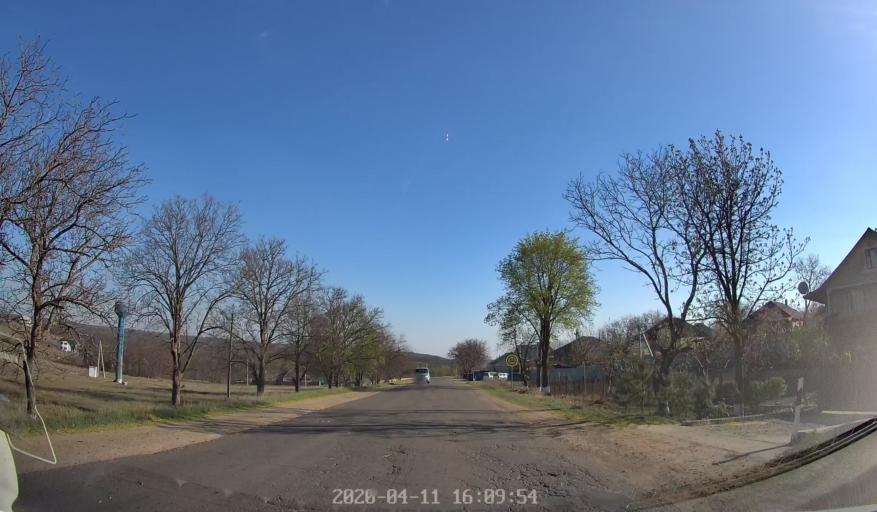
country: MD
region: Chisinau
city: Vadul lui Voda
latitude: 47.0709
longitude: 29.1364
